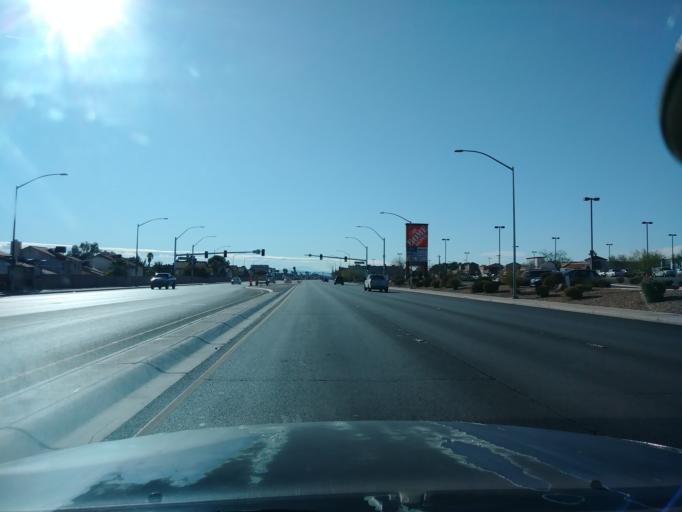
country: US
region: Nevada
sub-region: Clark County
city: Spring Valley
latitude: 36.1639
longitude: -115.2442
